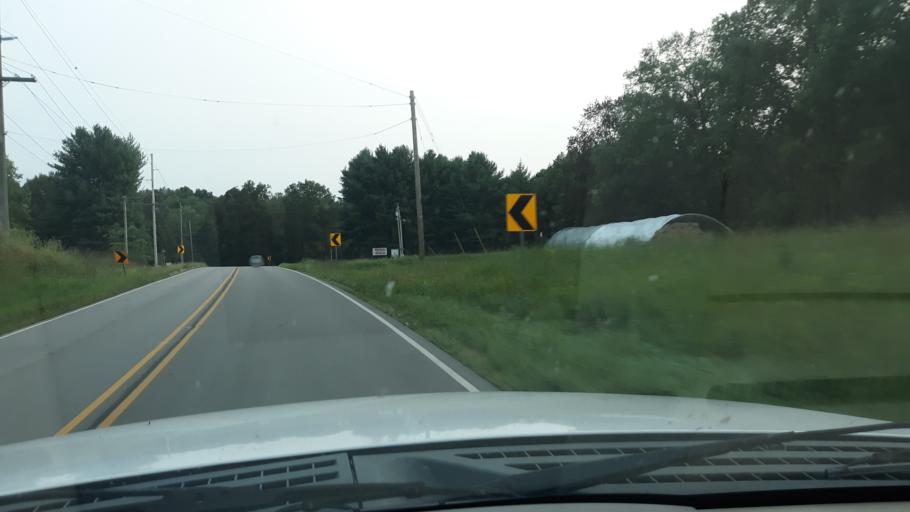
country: US
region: Illinois
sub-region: White County
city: Norris City
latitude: 37.9246
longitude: -88.3500
